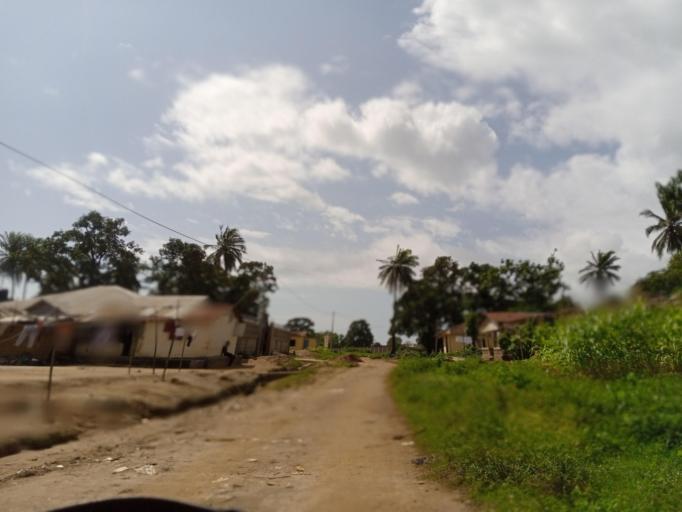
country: SL
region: Northern Province
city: Masoyila
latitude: 8.6083
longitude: -13.2053
